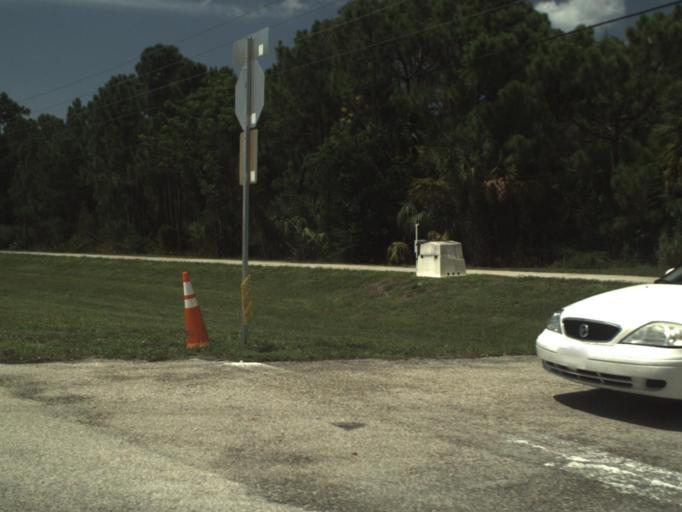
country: US
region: Florida
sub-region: Martin County
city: Port Salerno
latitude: 27.1371
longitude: -80.2089
